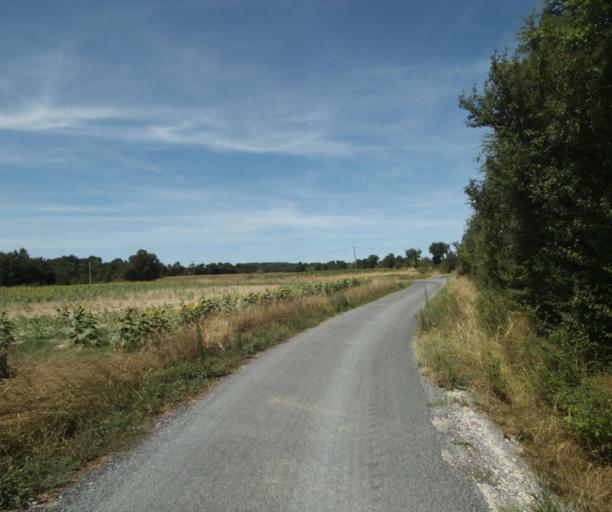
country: FR
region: Midi-Pyrenees
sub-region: Departement du Tarn
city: Puylaurens
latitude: 43.5344
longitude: 2.0024
